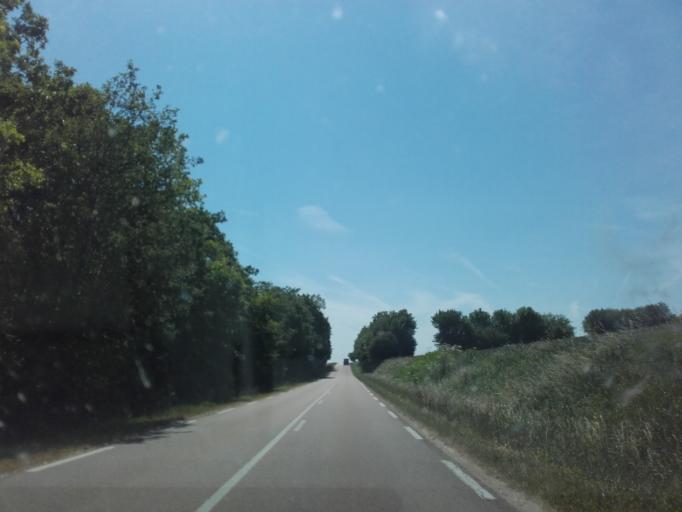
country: FR
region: Bourgogne
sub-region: Departement de l'Yonne
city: Chablis
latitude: 47.7363
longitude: 3.8438
